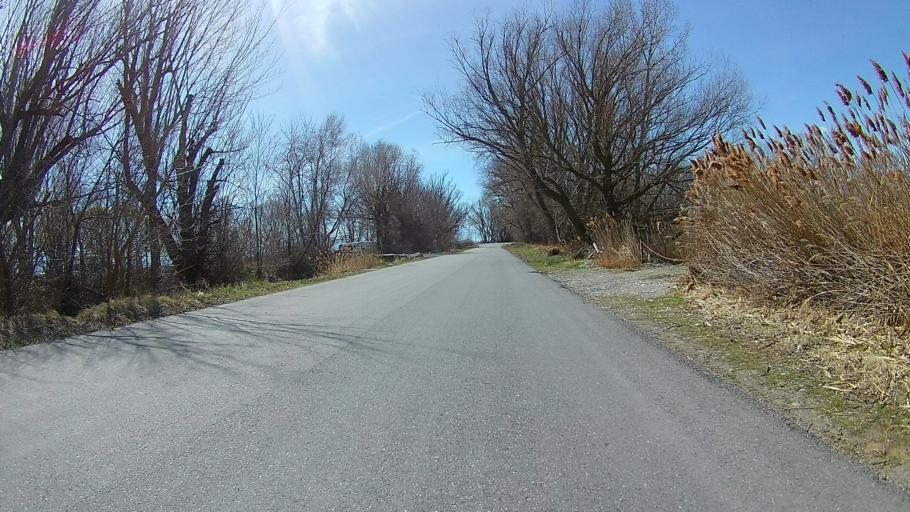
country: US
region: Utah
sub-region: Utah County
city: American Fork
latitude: 40.3456
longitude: -111.8017
